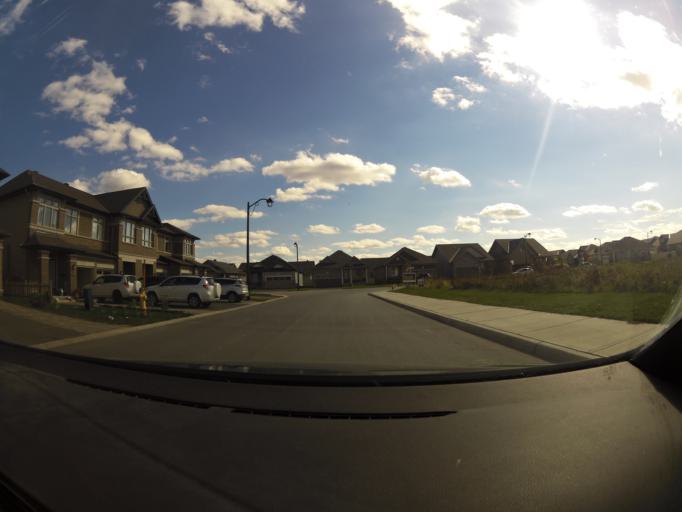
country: CA
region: Ontario
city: Bells Corners
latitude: 45.2719
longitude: -75.8898
